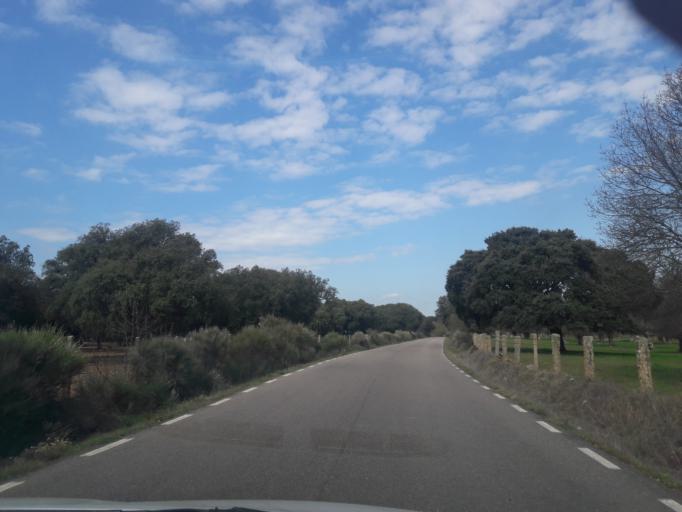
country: ES
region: Castille and Leon
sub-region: Provincia de Salamanca
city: Zamarra
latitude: 40.5552
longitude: -6.4487
